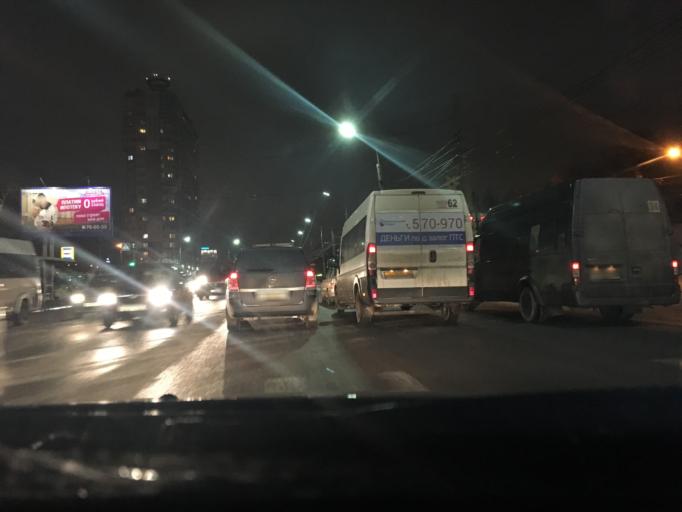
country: RU
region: Tula
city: Mendeleyevskiy
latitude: 54.1531
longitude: 37.5841
